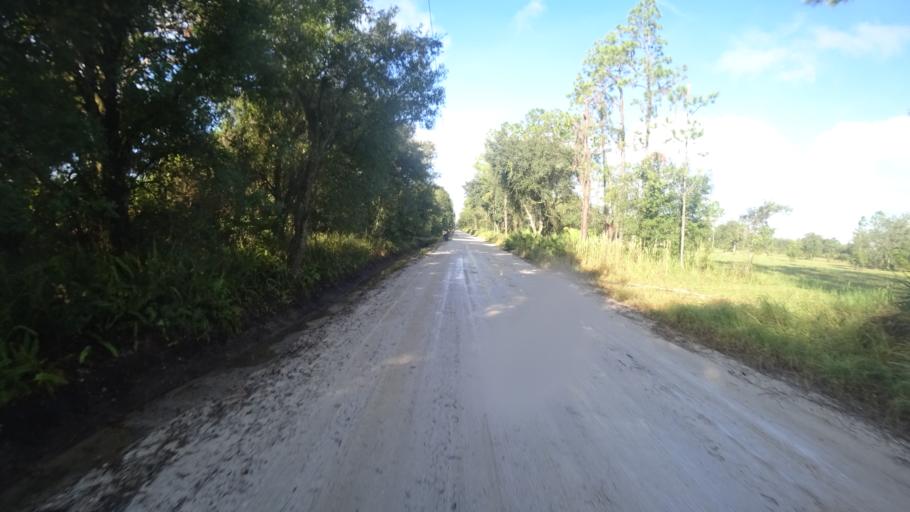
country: US
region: Florida
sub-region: Sarasota County
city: The Meadows
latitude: 27.4311
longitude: -82.3141
